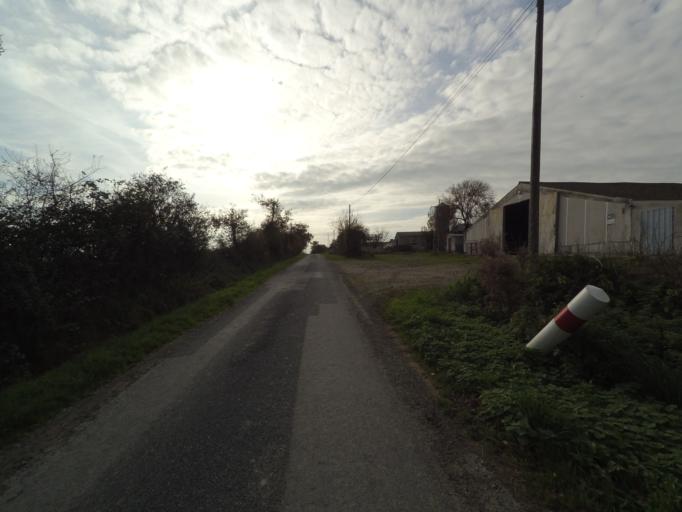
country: FR
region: Pays de la Loire
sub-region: Departement de la Vendee
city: Saint-Hilaire-de-Loulay
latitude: 47.0341
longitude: -1.3396
